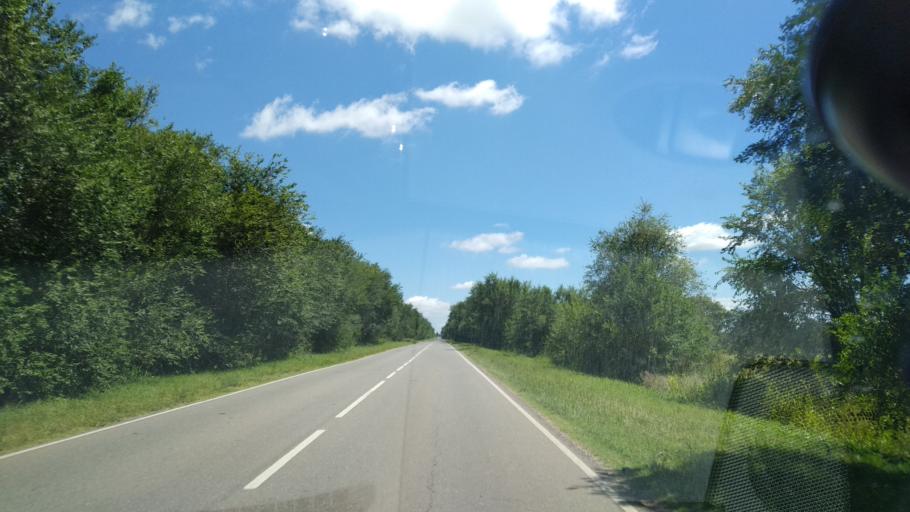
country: AR
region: Cordoba
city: Villa Cura Brochero
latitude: -31.5663
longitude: -65.1122
